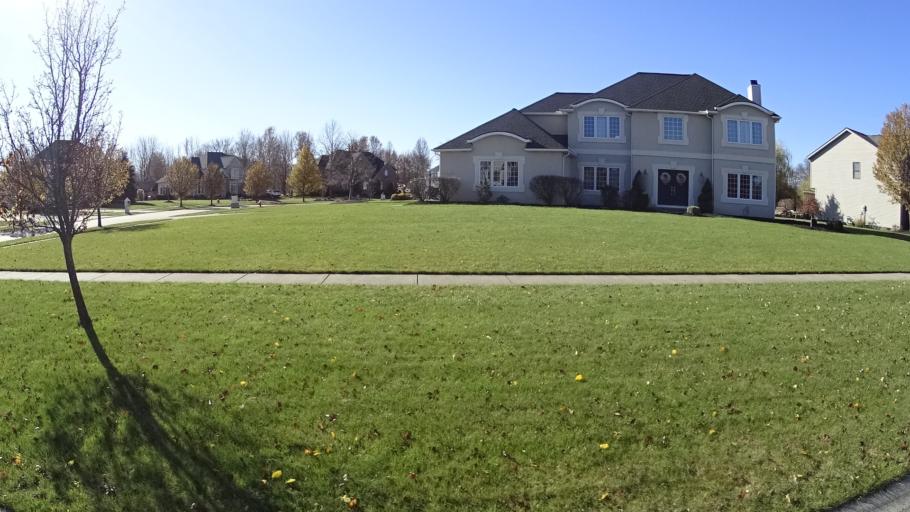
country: US
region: Ohio
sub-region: Lorain County
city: North Ridgeville
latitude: 41.4241
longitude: -82.0009
